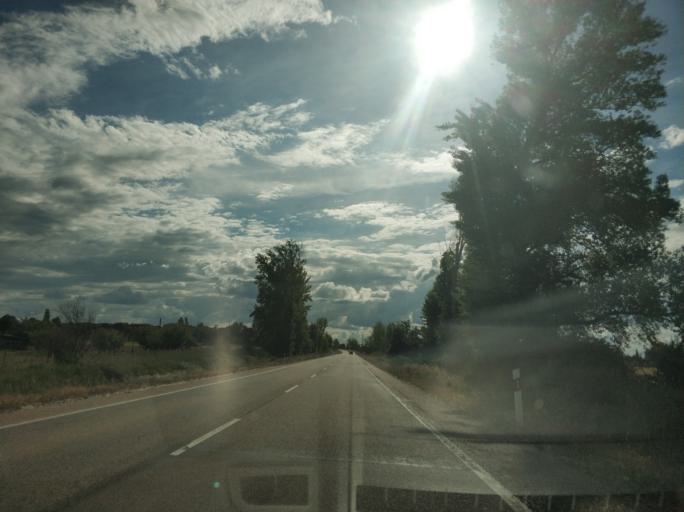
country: ES
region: Castille and Leon
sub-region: Provincia de Burgos
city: Villalba de Duero
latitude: 41.6619
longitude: -3.7502
